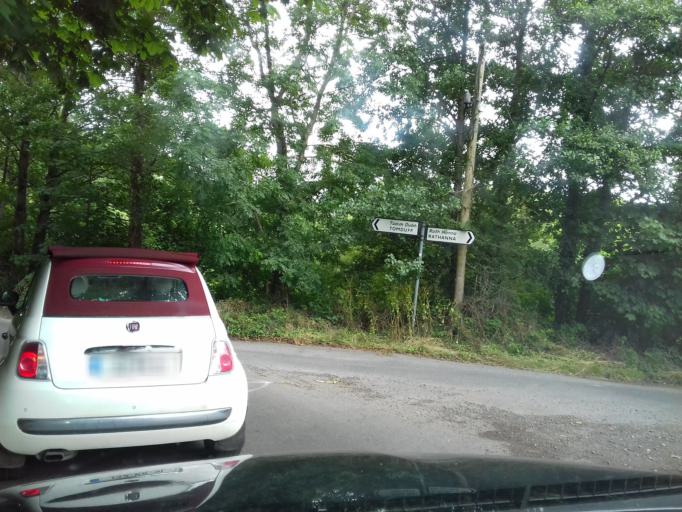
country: IE
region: Leinster
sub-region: Kilkenny
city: Graiguenamanagh
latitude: 52.6136
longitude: -6.8426
